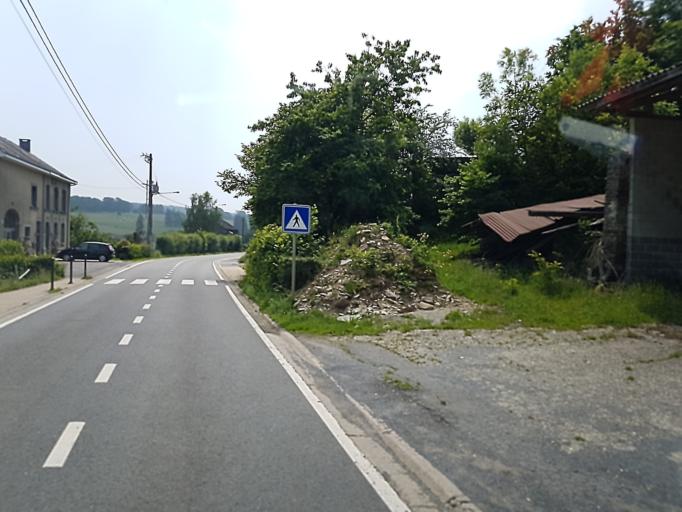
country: BE
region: Wallonia
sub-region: Province du Luxembourg
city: Manhay
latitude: 50.3225
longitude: 5.7319
